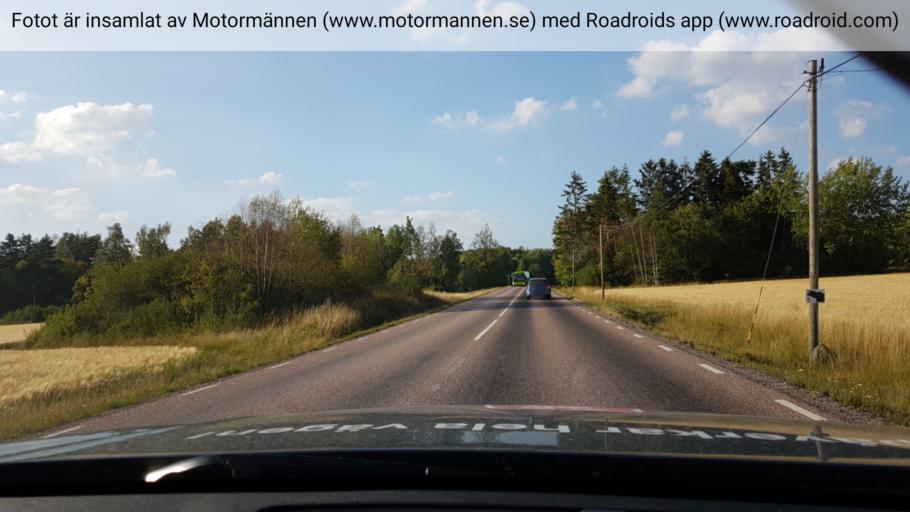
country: SE
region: Soedermanland
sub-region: Strangnas Kommun
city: Stallarholmen
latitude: 59.3287
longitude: 17.2253
